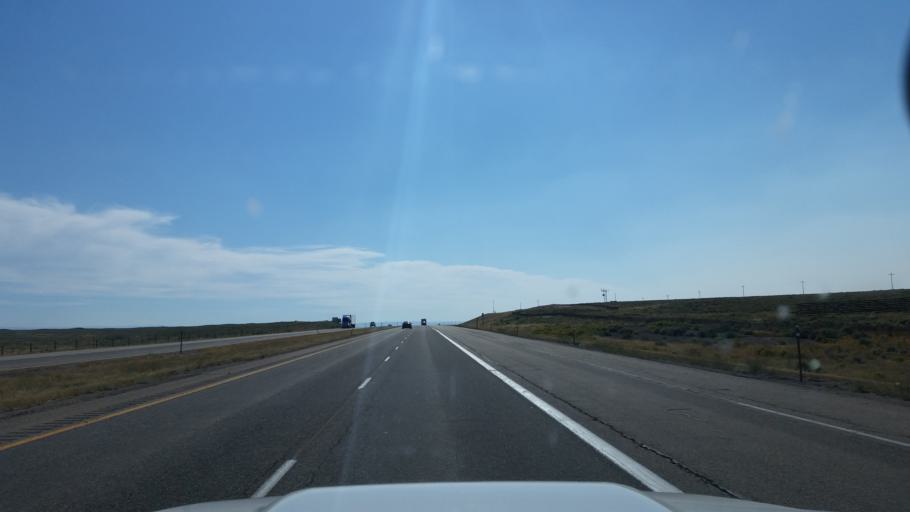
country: US
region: Wyoming
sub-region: Uinta County
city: Lyman
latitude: 41.4321
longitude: -110.1120
